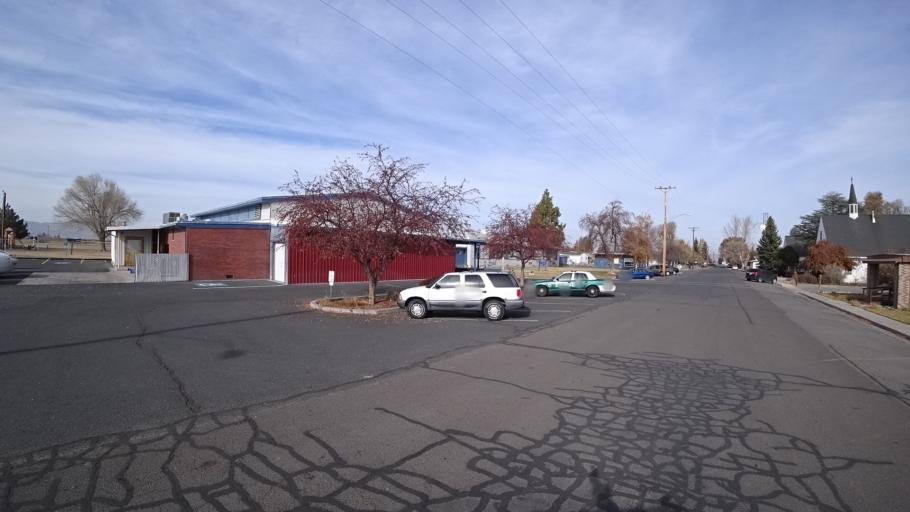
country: US
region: California
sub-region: Siskiyou County
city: Tulelake
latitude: 41.9549
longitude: -121.4780
